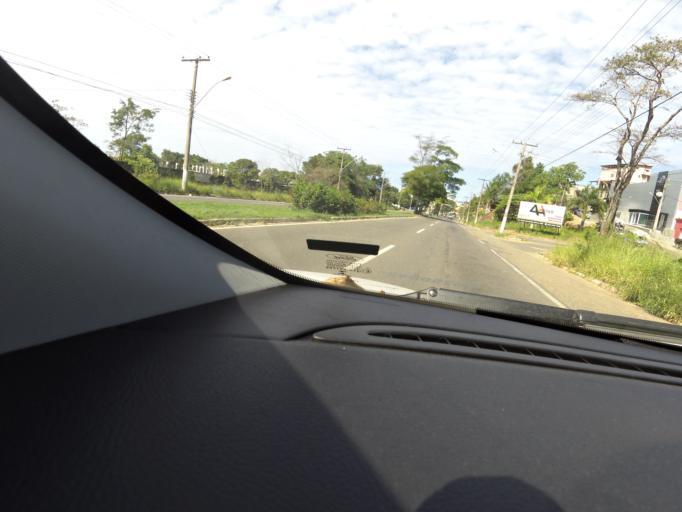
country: BR
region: Espirito Santo
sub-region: Guarapari
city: Guarapari
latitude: -20.6505
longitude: -40.5069
